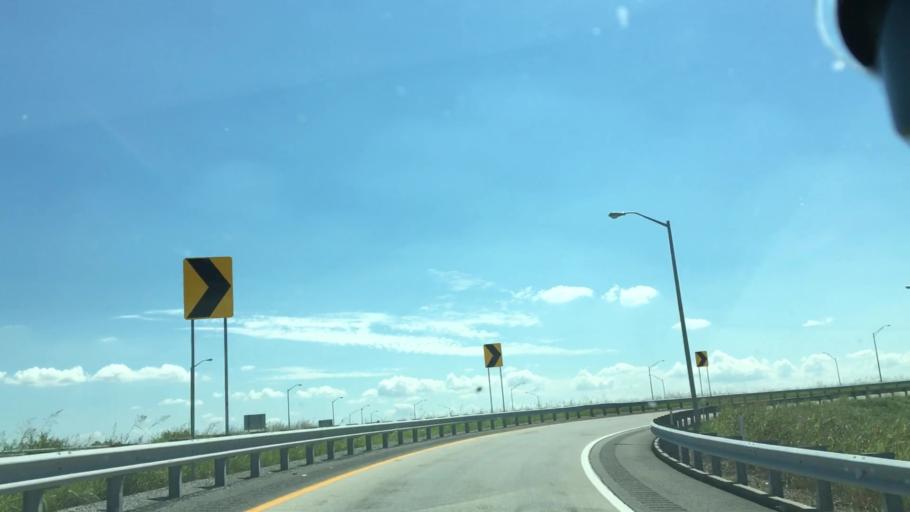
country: US
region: Kentucky
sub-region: Christian County
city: Oak Grove
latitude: 36.7036
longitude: -87.4528
